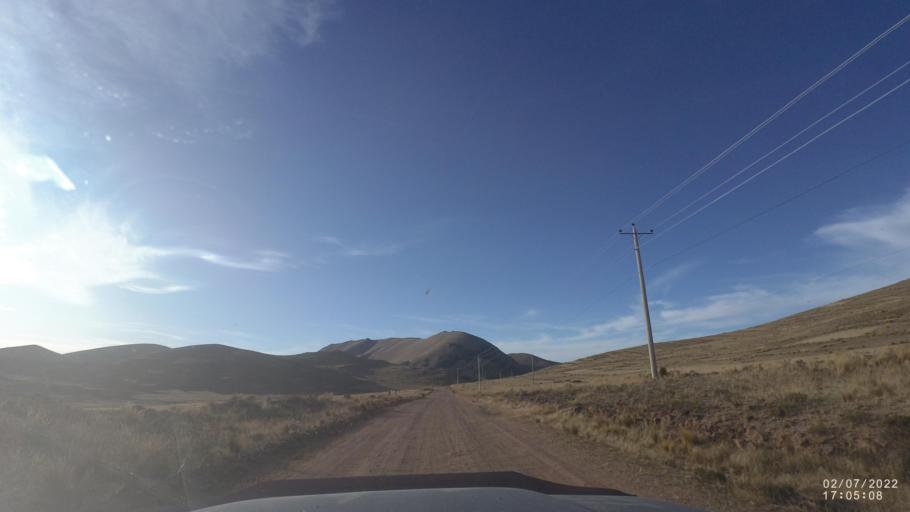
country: BO
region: Cochabamba
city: Irpa Irpa
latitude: -17.9095
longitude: -66.5598
